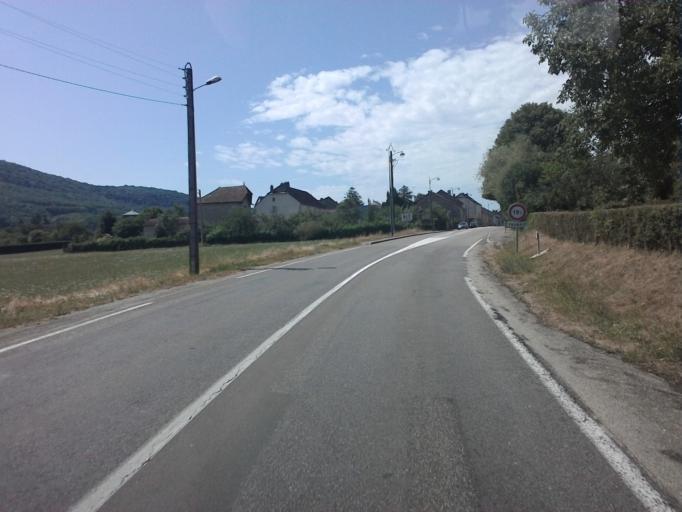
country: FR
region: Franche-Comte
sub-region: Departement du Jura
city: Cousance
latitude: 46.5770
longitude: 5.4394
